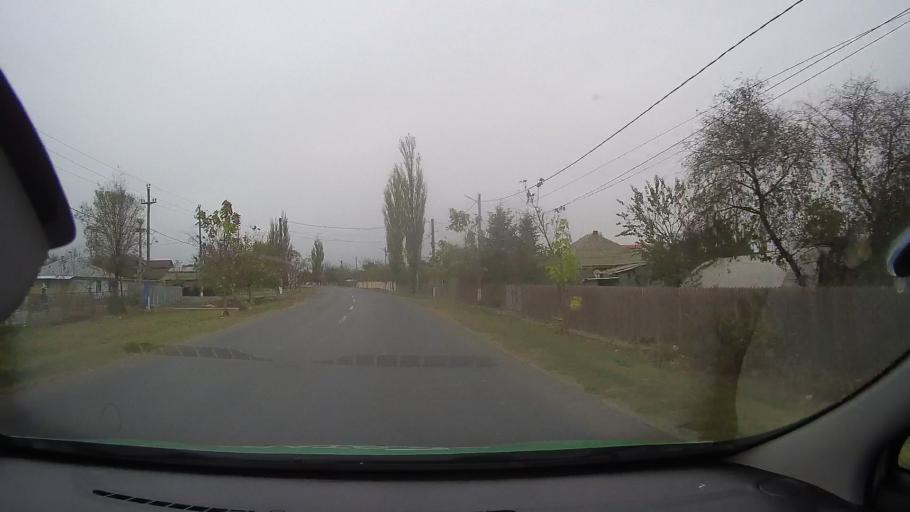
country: RO
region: Ialomita
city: Tandarei
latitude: 44.6542
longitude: 27.6543
